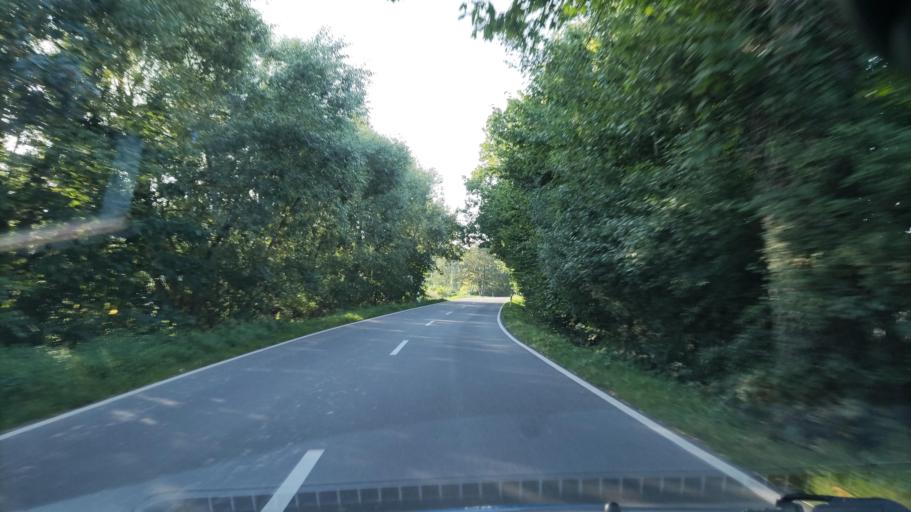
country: DE
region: Schleswig-Holstein
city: Ahrensbok
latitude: 54.0294
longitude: 10.5575
